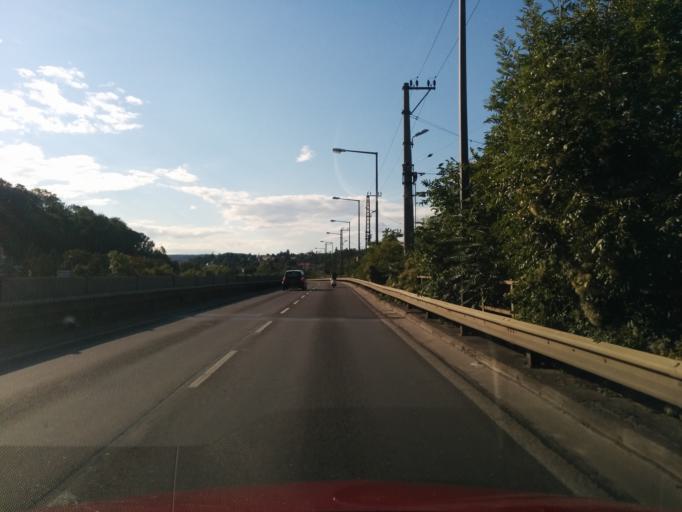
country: AT
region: Lower Austria
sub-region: Politischer Bezirk Modling
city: Perchtoldsdorf
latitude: 48.1984
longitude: 16.2559
